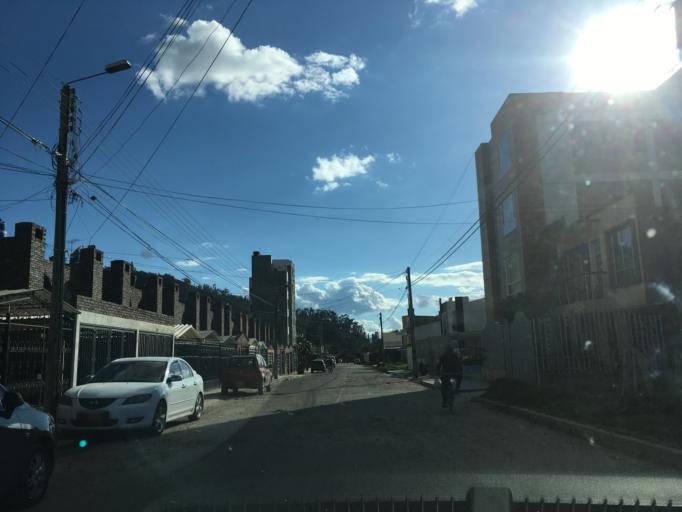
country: CO
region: Boyaca
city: Sogamoso
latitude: 5.7067
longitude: -72.9336
